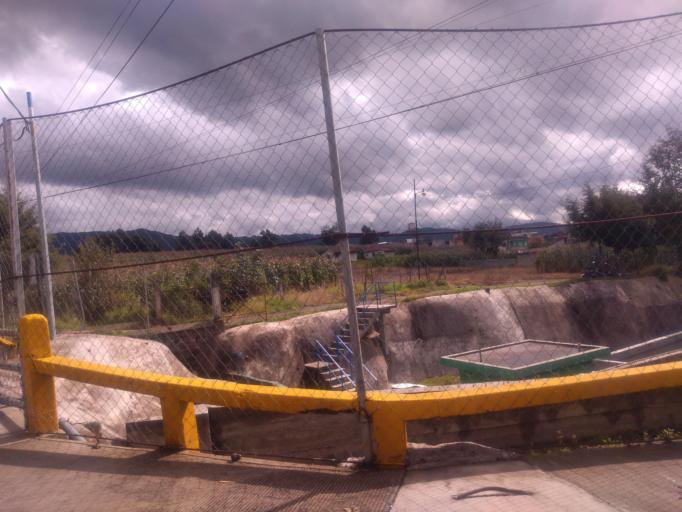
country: GT
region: Quetzaltenango
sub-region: Municipio de La Esperanza
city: La Esperanza
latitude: 14.8679
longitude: -91.5589
